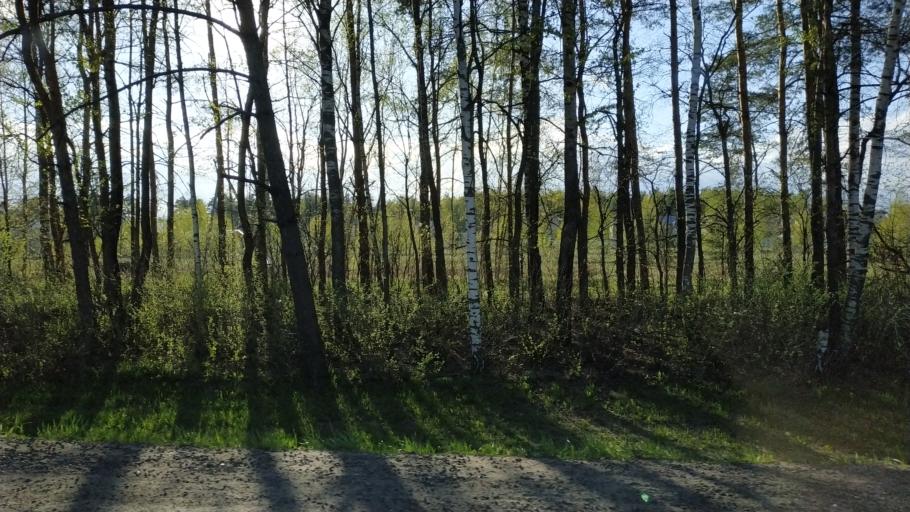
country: RU
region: Moskovskaya
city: Gzhel'
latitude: 55.6426
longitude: 38.3694
